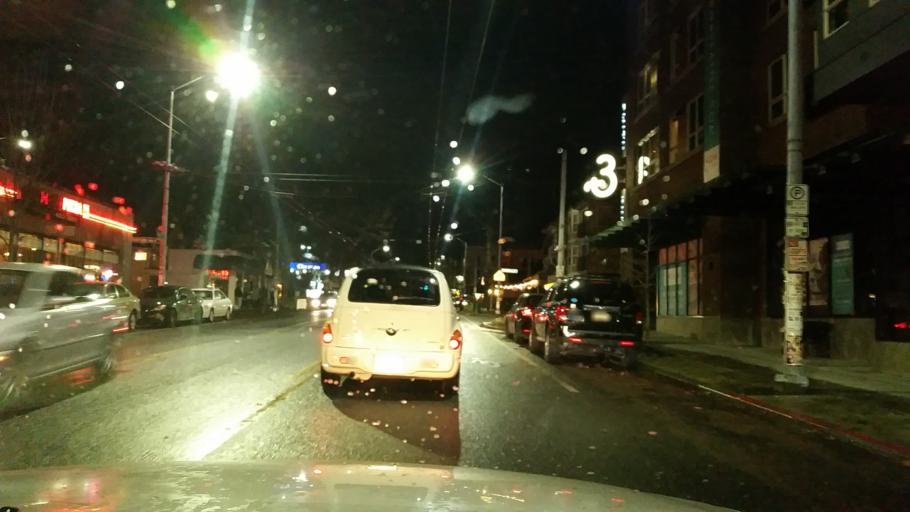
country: US
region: Washington
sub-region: King County
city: Seattle
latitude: 47.6613
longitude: -122.3413
